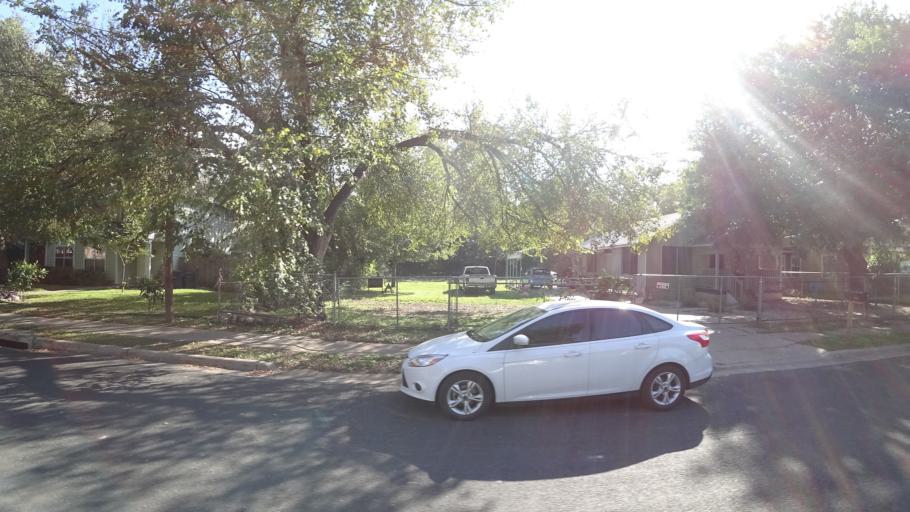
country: US
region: Texas
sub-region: Travis County
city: Austin
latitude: 30.2607
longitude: -97.7289
